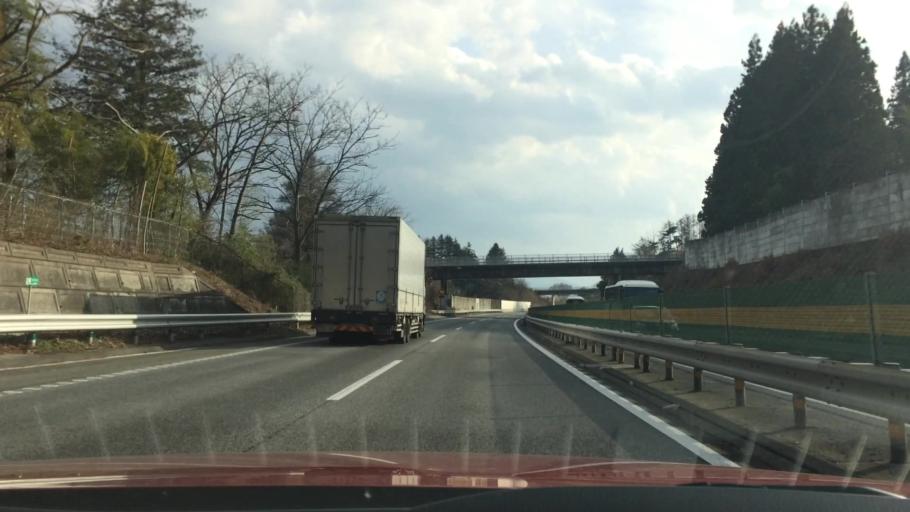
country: JP
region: Nagano
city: Ina
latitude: 35.8091
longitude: 137.9280
